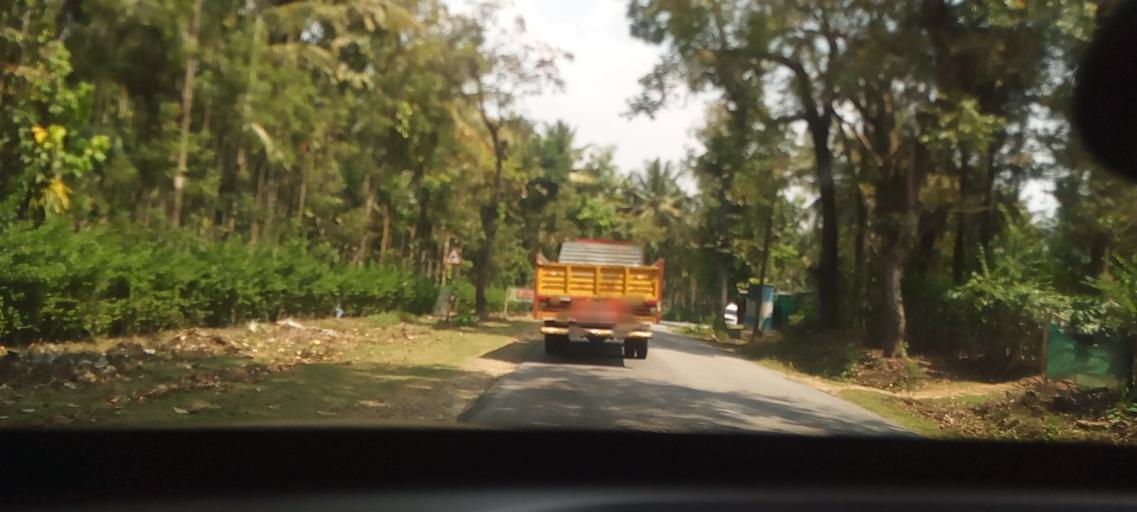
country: IN
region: Karnataka
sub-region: Chikmagalur
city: Chikmagalur
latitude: 13.3324
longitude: 75.5562
